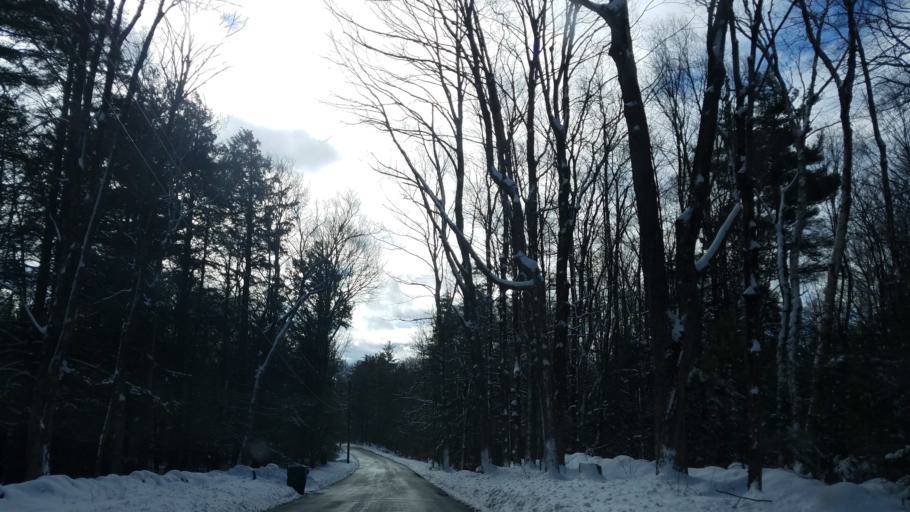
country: US
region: Connecticut
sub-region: Litchfield County
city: Winchester Center
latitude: 41.9685
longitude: -73.1202
